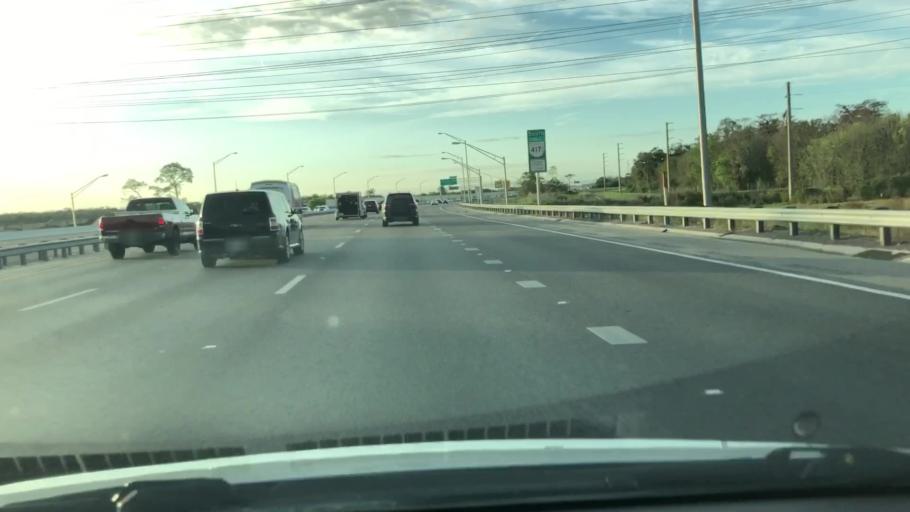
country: US
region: Florida
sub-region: Orange County
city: Azalea Park
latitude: 28.5030
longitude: -81.2450
